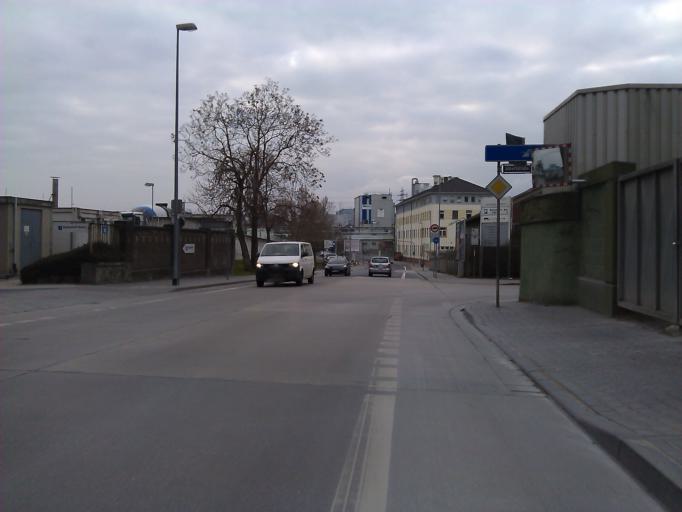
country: DE
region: Hesse
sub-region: Regierungsbezirk Darmstadt
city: Wiesbaden
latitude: 50.0311
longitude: 8.2519
